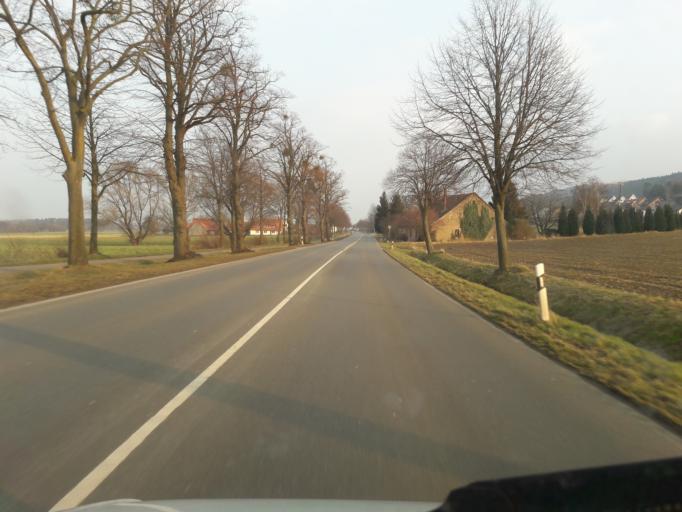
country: DE
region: North Rhine-Westphalia
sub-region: Regierungsbezirk Detmold
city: Huellhorst
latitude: 52.3086
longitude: 8.6790
